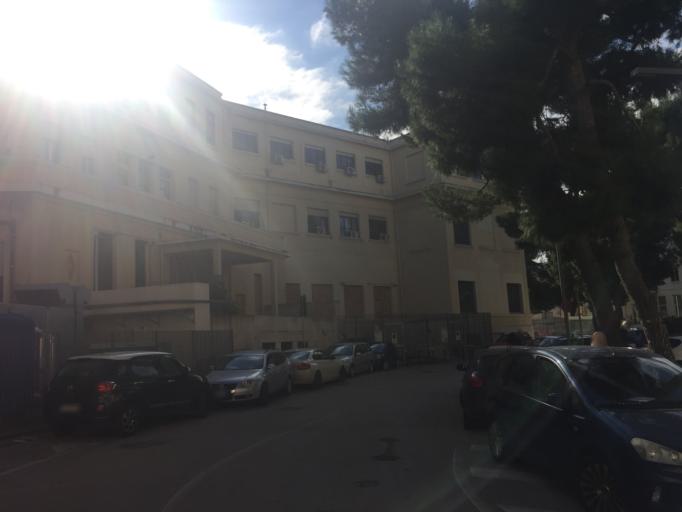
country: IT
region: Apulia
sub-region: Provincia di Bari
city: Bari
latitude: 41.1119
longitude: 16.8592
